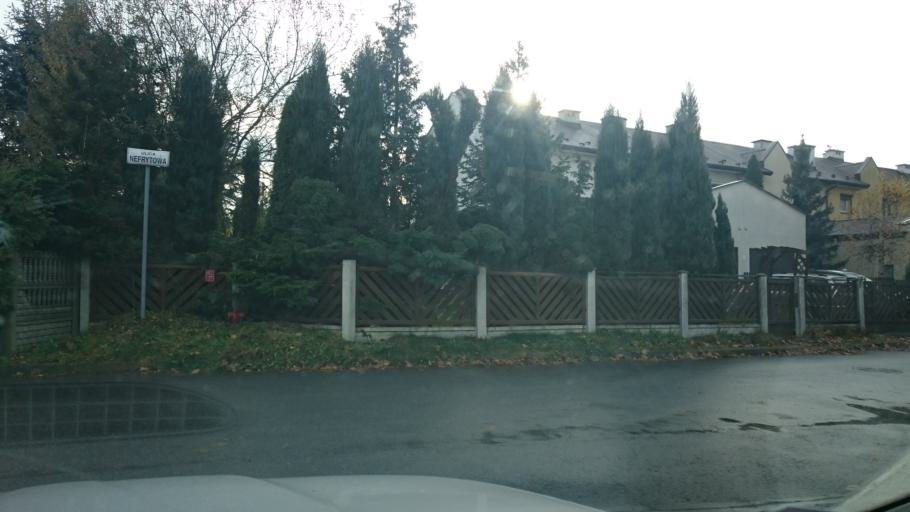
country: PL
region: Lesser Poland Voivodeship
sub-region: Powiat wielicki
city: Czarnochowice
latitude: 50.0208
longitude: 20.0491
